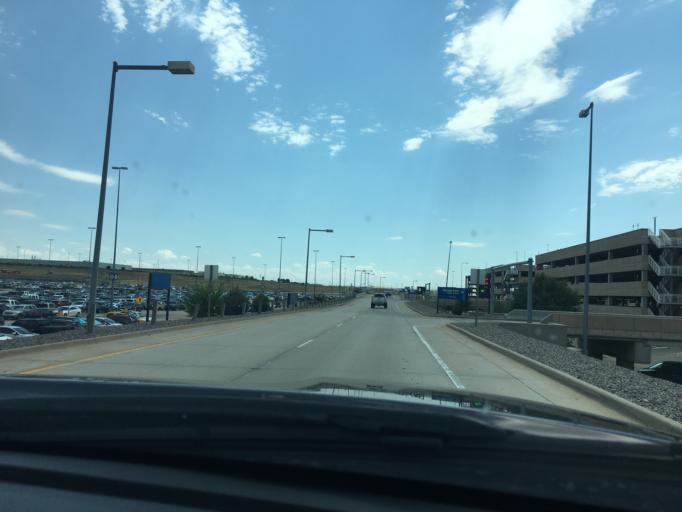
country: US
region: Colorado
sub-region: Weld County
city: Lochbuie
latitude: 39.8496
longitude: -104.6698
